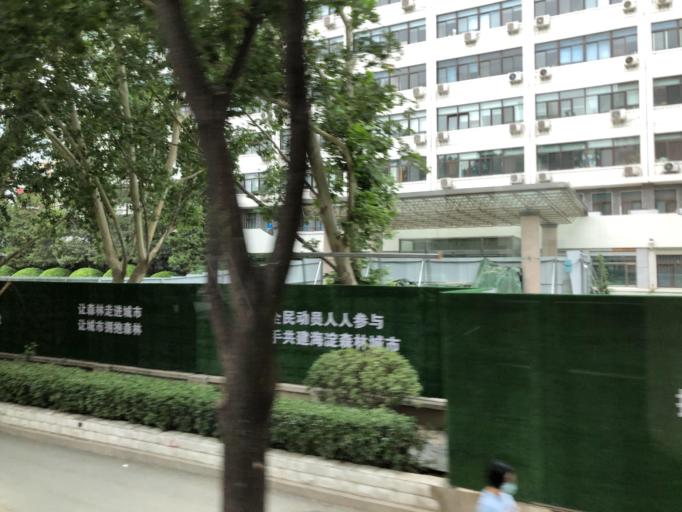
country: CN
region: Beijing
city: Jinrongjie
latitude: 39.9506
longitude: 116.3225
